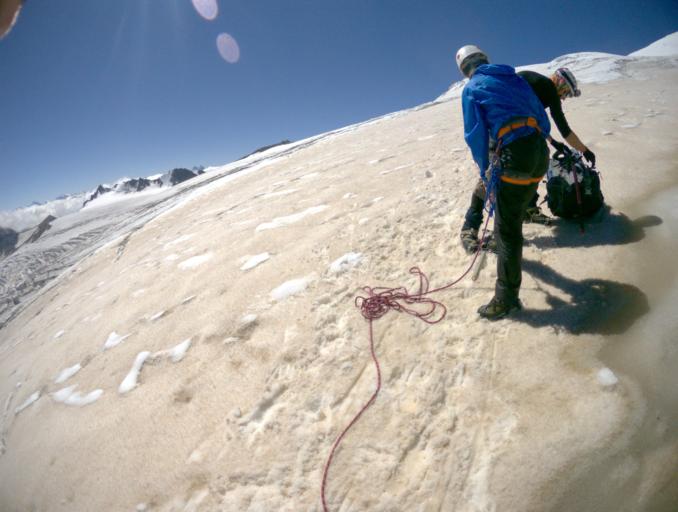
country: RU
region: Kabardino-Balkariya
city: Terskol
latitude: 43.3615
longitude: 42.4990
